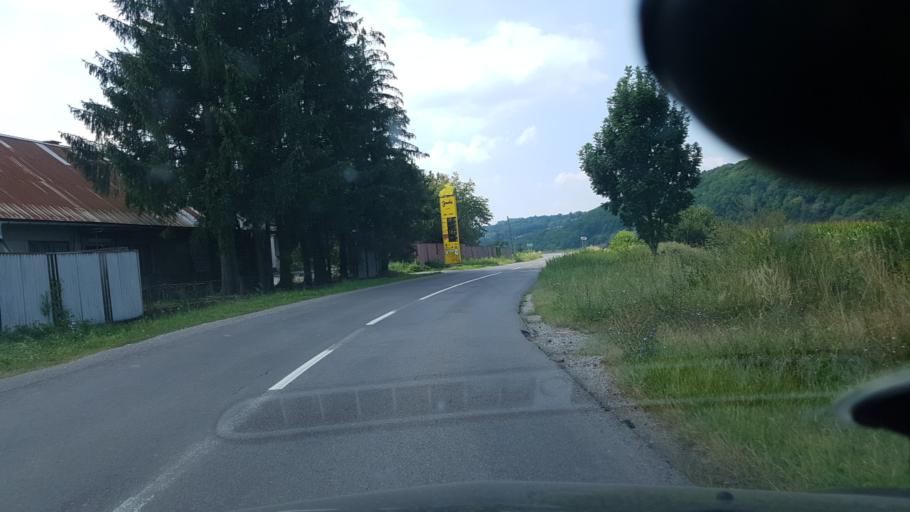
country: SK
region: Banskobystricky
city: Hrochot,Slovakia
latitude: 48.6555
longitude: 19.2462
